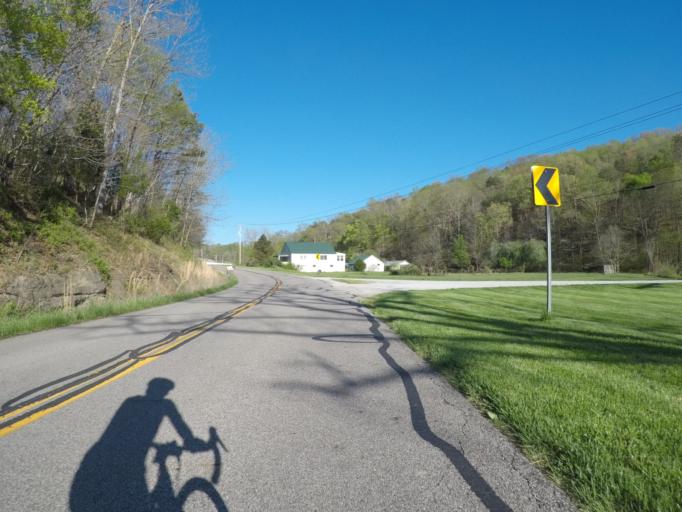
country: US
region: Kentucky
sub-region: Boyd County
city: Meads
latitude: 38.3634
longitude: -82.6768
